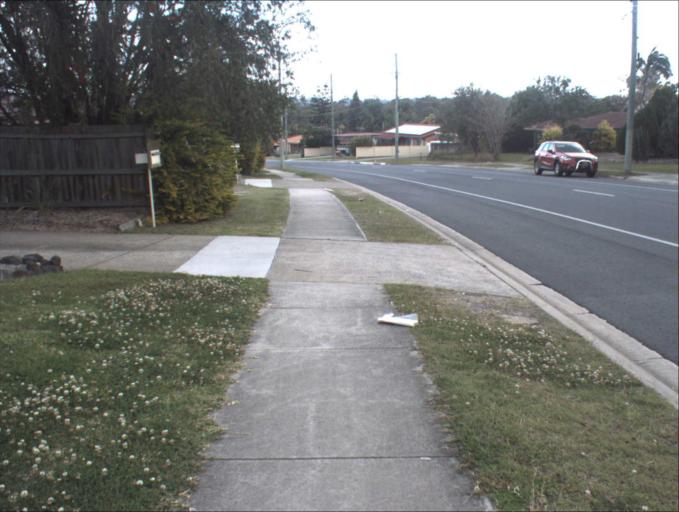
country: AU
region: Queensland
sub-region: Logan
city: Park Ridge South
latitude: -27.6717
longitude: 153.0371
